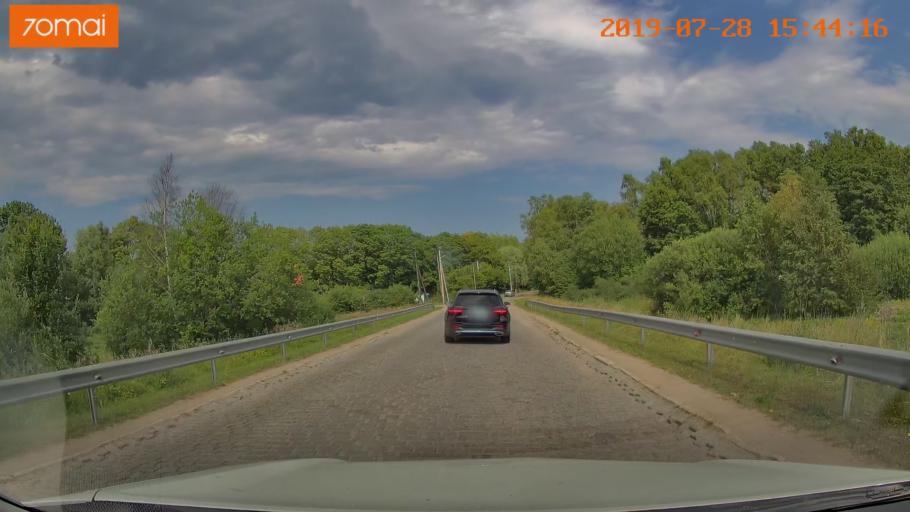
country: RU
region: Kaliningrad
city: Donskoye
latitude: 54.9395
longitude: 20.0296
